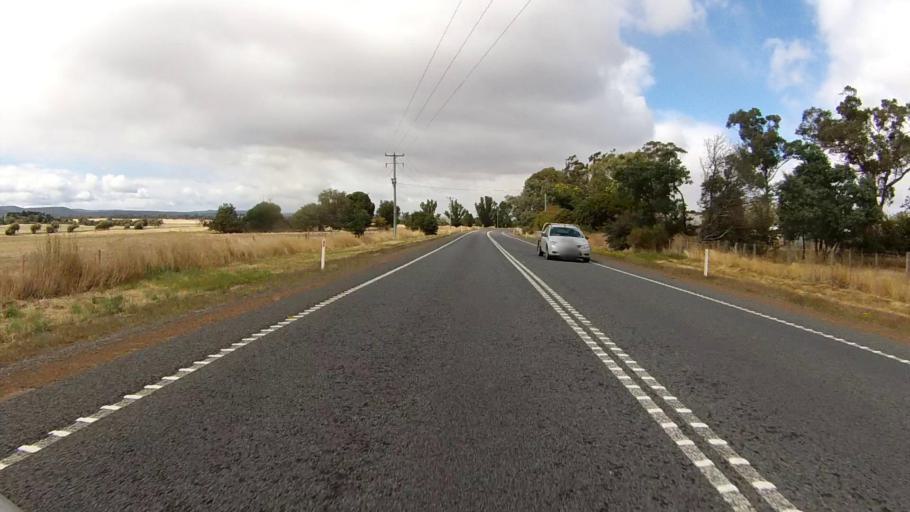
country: AU
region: Tasmania
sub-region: Northern Midlands
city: Evandale
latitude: -41.9834
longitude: 147.5062
